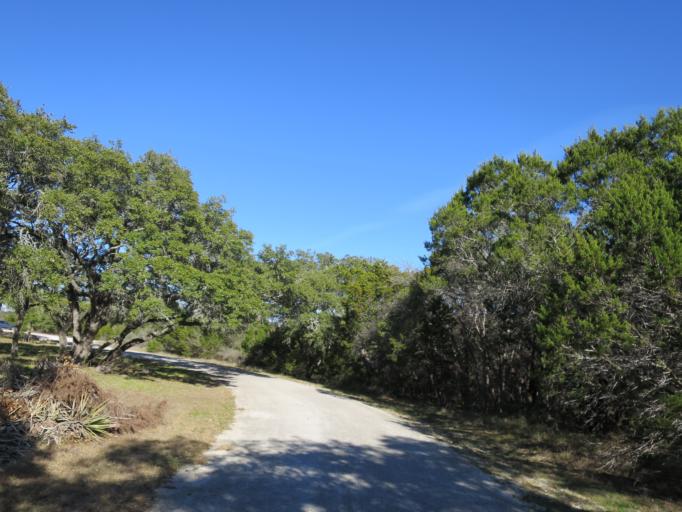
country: US
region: Texas
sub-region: Llano County
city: Kingsland
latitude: 30.6835
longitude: -98.3521
